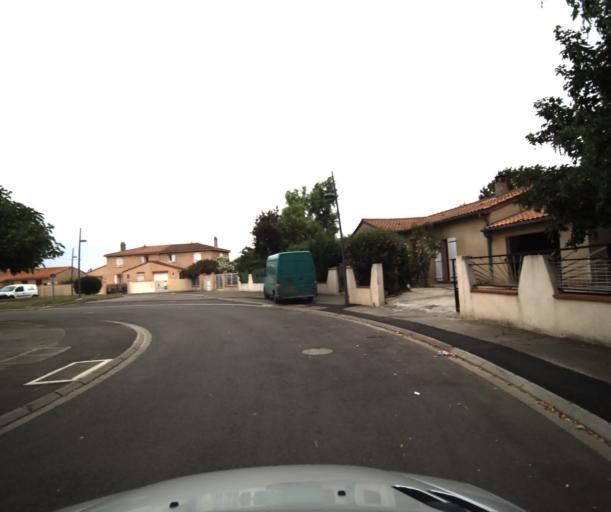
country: FR
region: Midi-Pyrenees
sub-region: Departement de la Haute-Garonne
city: Portet-sur-Garonne
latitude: 43.5436
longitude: 1.4141
